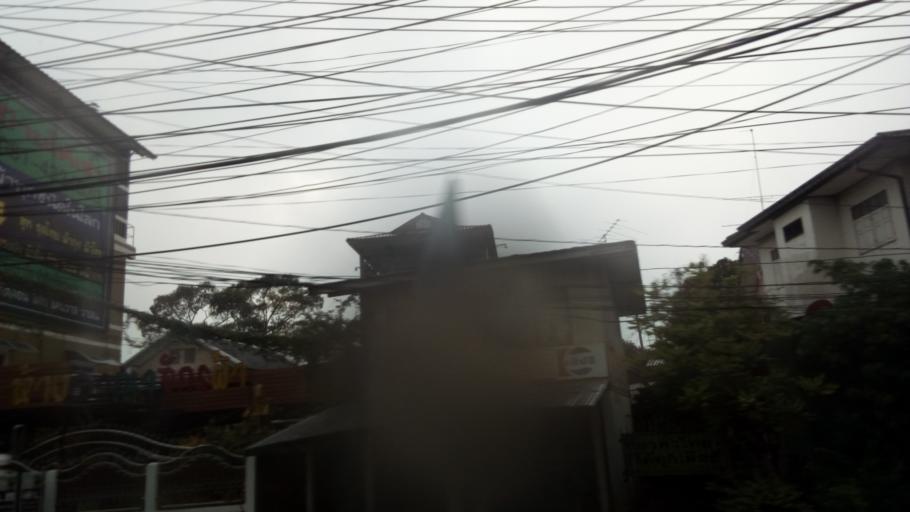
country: TH
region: Phra Nakhon Si Ayutthaya
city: Phra Nakhon Si Ayutthaya
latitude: 14.3518
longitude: 100.5835
